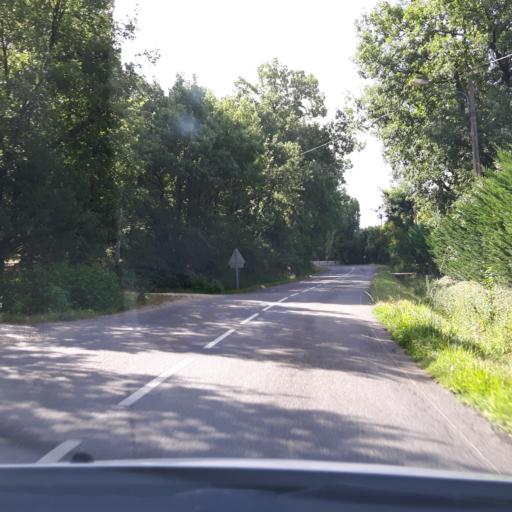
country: FR
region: Midi-Pyrenees
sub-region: Departement de la Haute-Garonne
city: Bouloc
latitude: 43.7968
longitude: 1.4129
